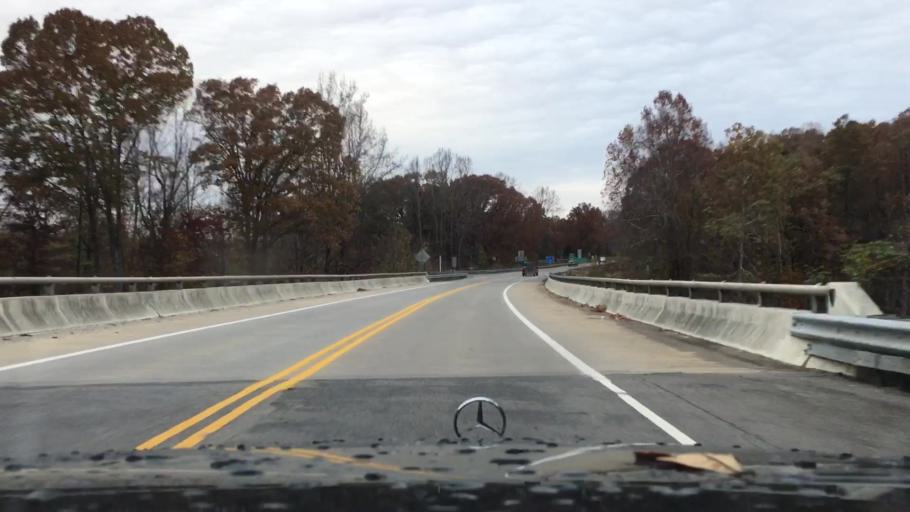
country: US
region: Virginia
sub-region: Campbell County
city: Altavista
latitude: 37.1277
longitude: -79.3069
